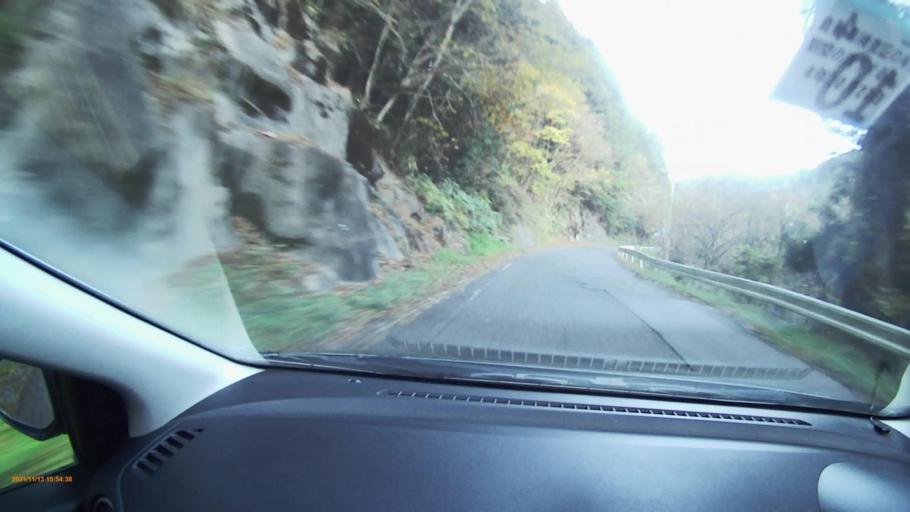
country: JP
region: Gifu
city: Nakatsugawa
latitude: 35.5958
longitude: 137.4451
